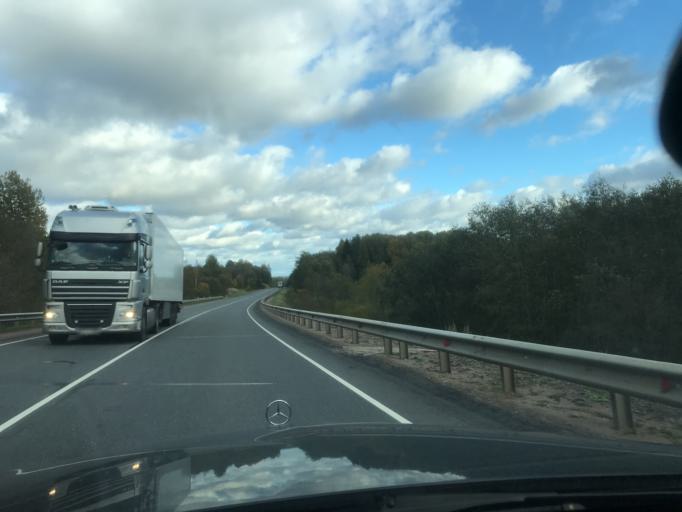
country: RU
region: Pskov
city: Novosokol'niki
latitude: 56.3485
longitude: 29.9199
